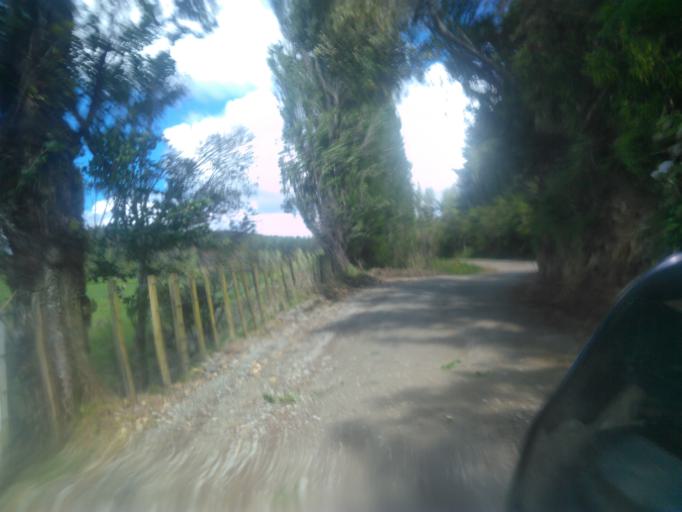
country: NZ
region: Hawke's Bay
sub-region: Wairoa District
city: Wairoa
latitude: -38.7682
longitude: 177.5953
